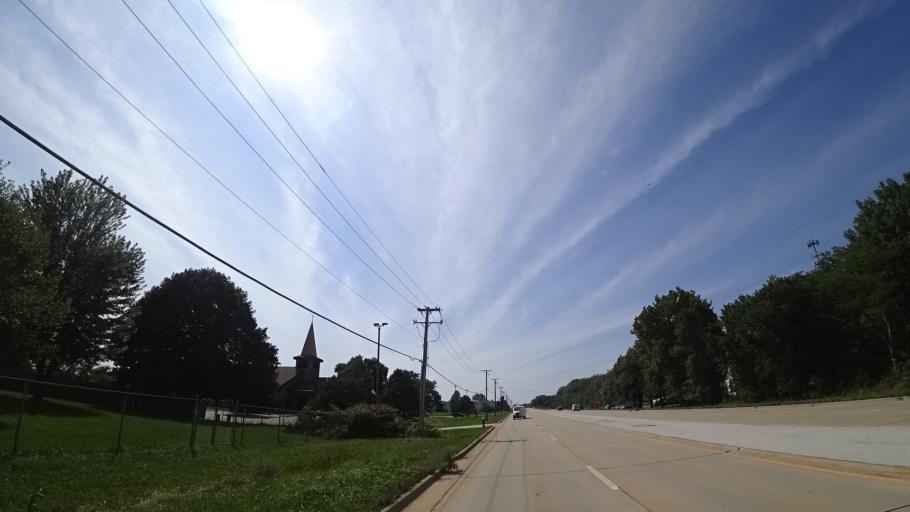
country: US
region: Illinois
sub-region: Will County
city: Frankfort Square
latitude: 41.5280
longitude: -87.7652
